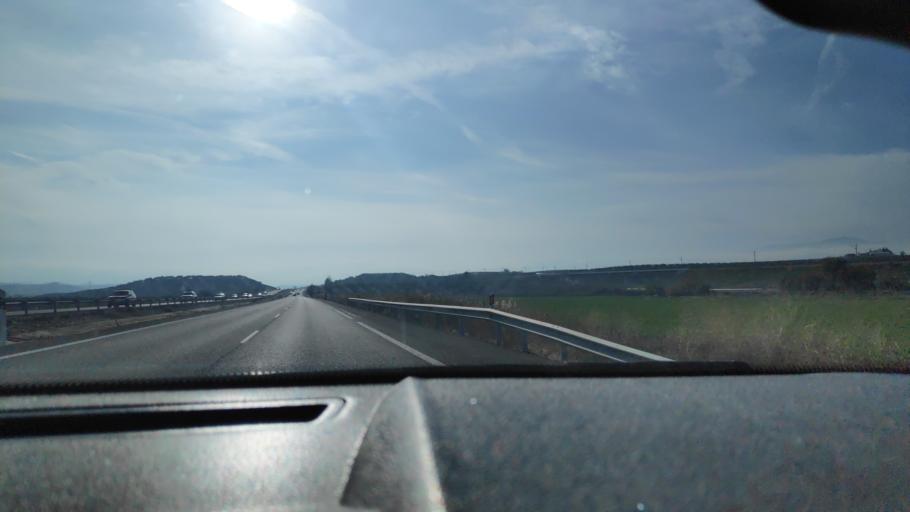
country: ES
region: Andalusia
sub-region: Provincia de Jaen
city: Mengibar
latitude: 37.8792
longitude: -3.7704
